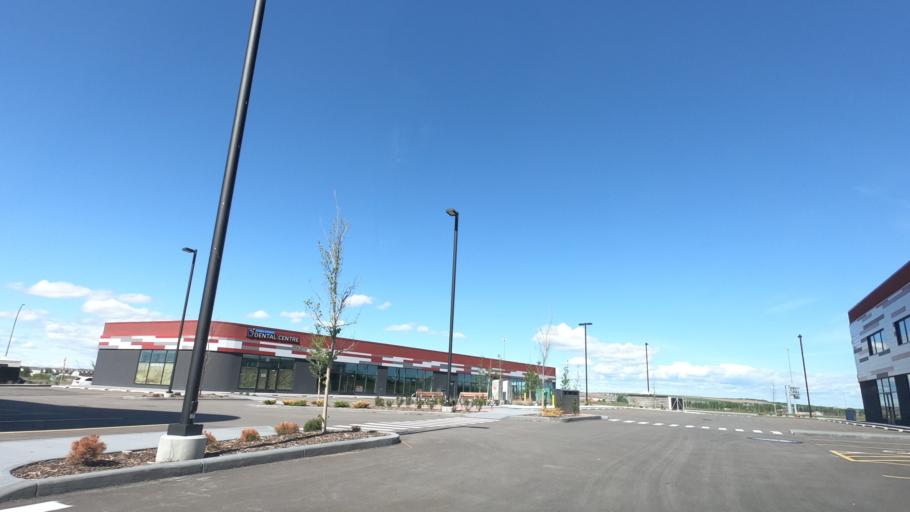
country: CA
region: Alberta
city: Airdrie
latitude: 51.2683
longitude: -113.9981
